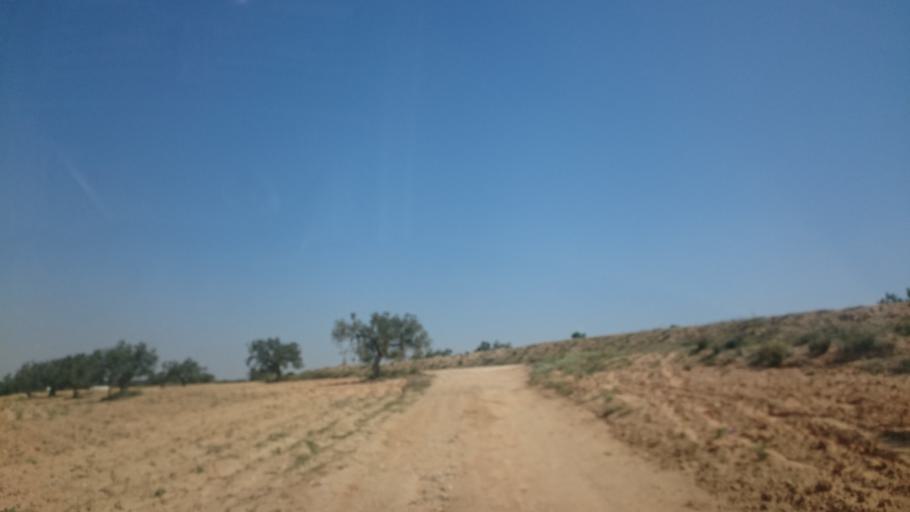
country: TN
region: Safaqis
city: Sfax
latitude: 34.7935
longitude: 10.5514
